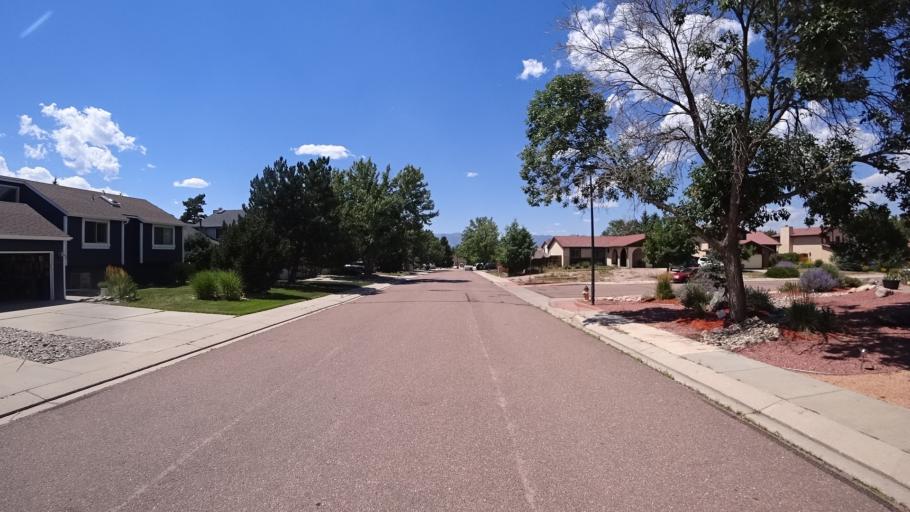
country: US
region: Colorado
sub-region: El Paso County
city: Black Forest
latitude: 38.9535
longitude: -104.7531
